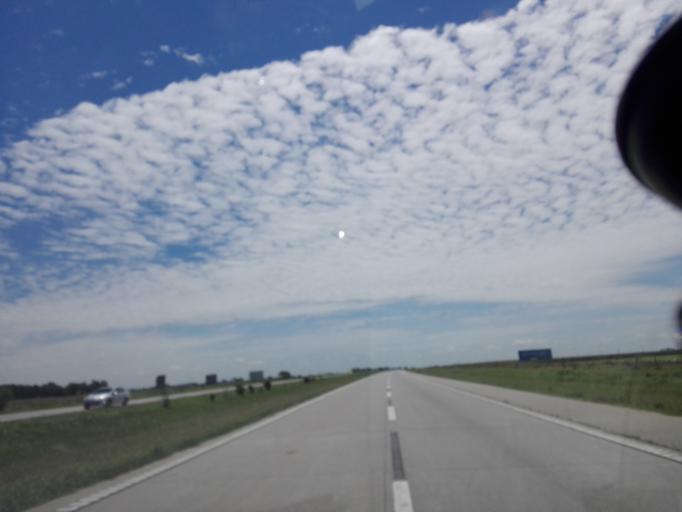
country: AR
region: Cordoba
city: Villa Maria
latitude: -32.3461
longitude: -63.2498
